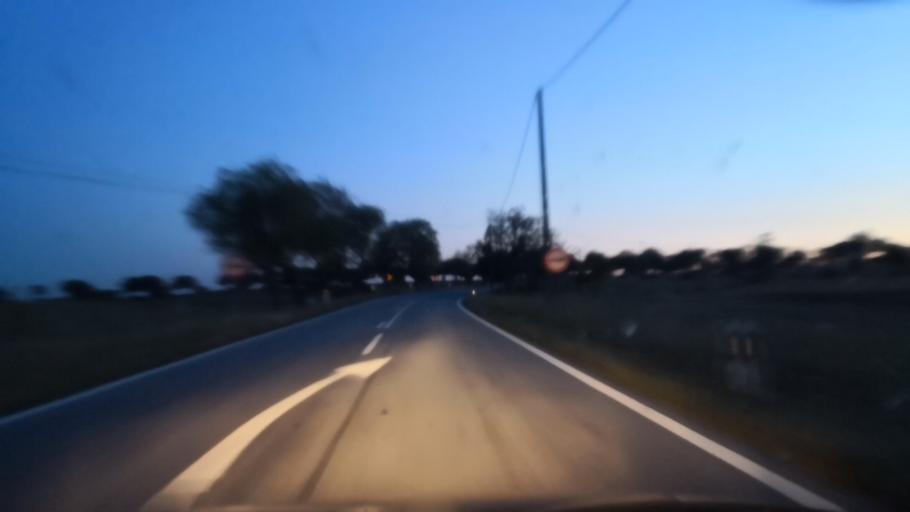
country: ES
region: Extremadura
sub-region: Provincia de Caceres
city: Piedras Albas
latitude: 39.8545
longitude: -7.0464
